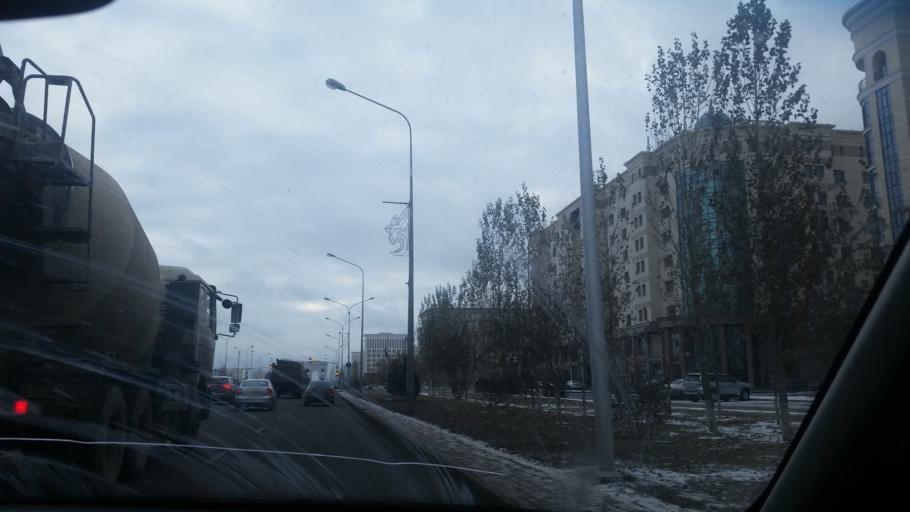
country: KZ
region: Astana Qalasy
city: Astana
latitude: 51.1105
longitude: 71.4321
